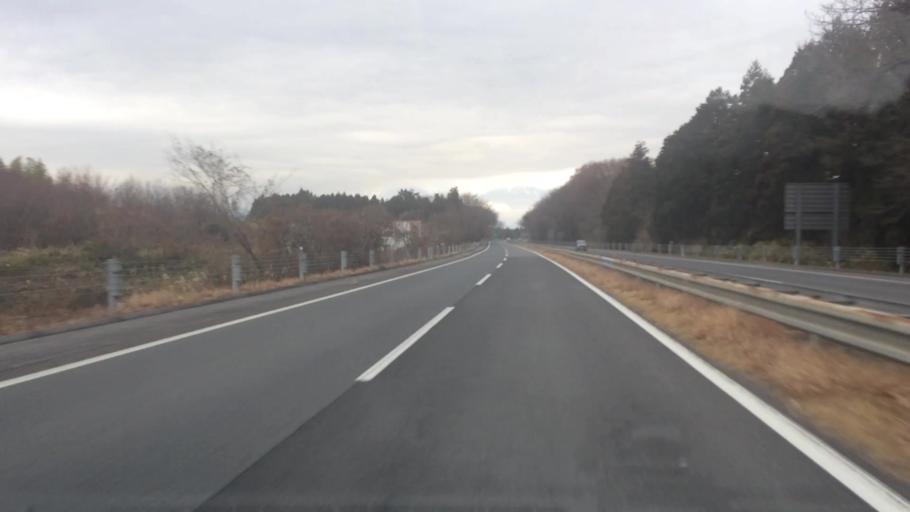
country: JP
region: Tochigi
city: Imaichi
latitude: 36.6921
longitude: 139.7483
